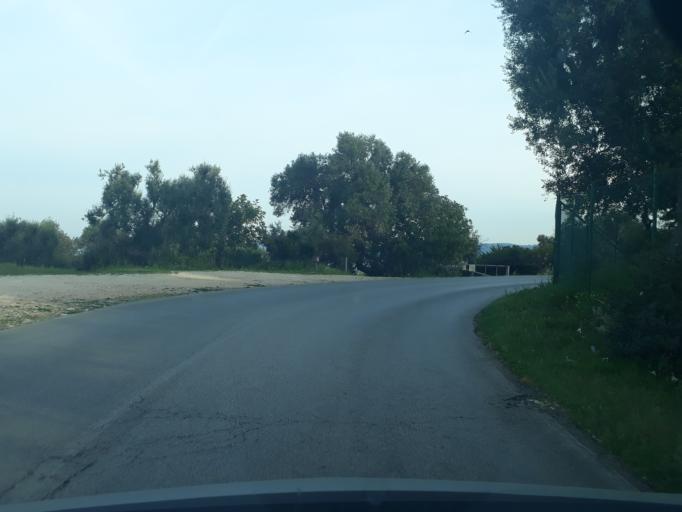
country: IT
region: Apulia
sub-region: Provincia di Brindisi
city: Fasano
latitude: 40.8333
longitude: 17.3449
